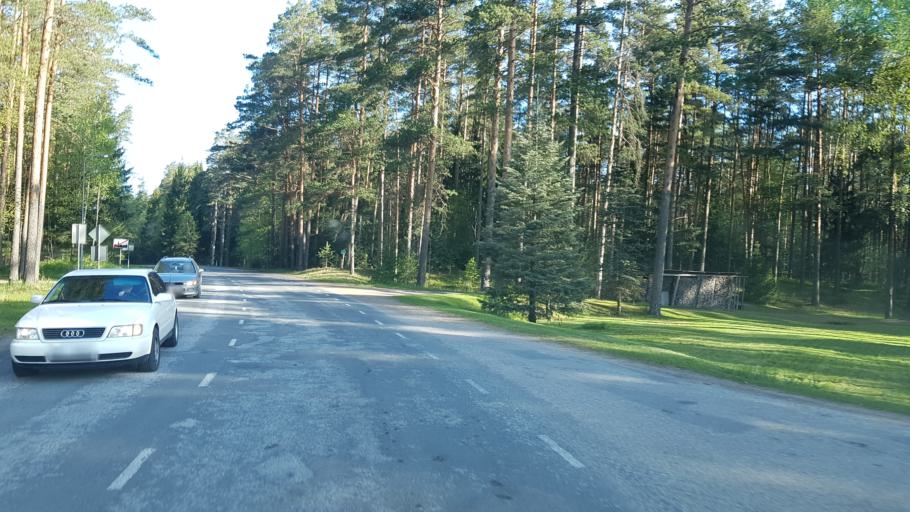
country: EE
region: Paernumaa
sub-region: Saarde vald
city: Kilingi-Nomme
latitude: 58.1509
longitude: 24.9390
